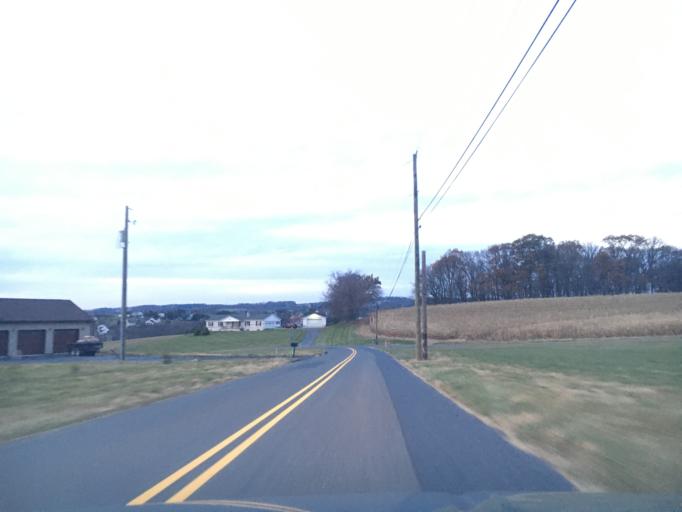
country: US
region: Pennsylvania
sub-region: Lehigh County
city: Schnecksville
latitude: 40.6945
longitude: -75.5792
